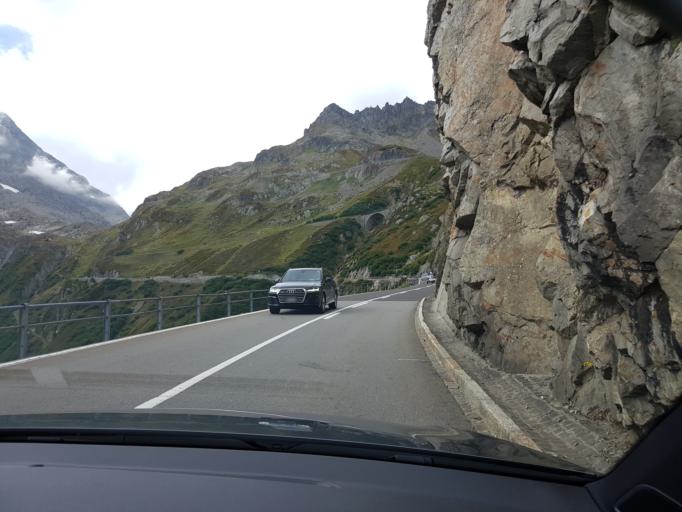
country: CH
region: Obwalden
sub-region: Obwalden
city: Engelberg
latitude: 46.7393
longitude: 8.4587
